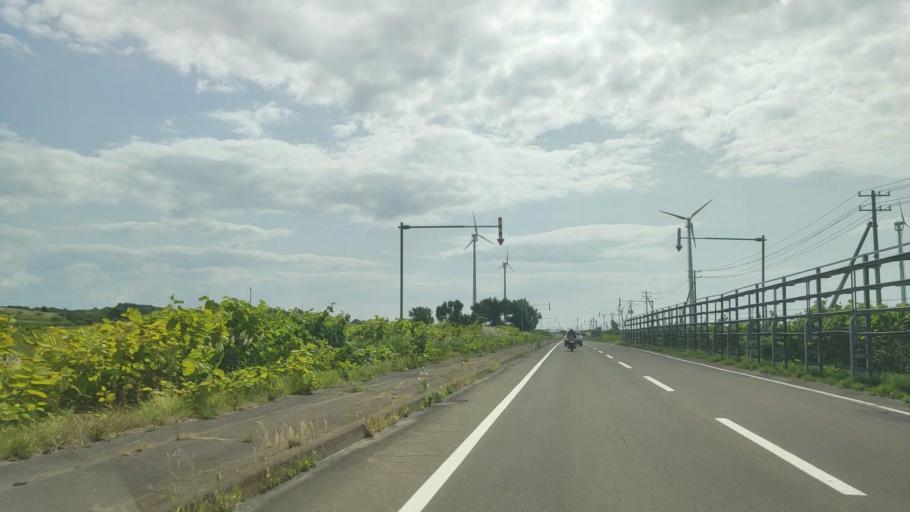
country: JP
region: Hokkaido
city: Rumoi
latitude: 44.3920
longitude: 141.7169
